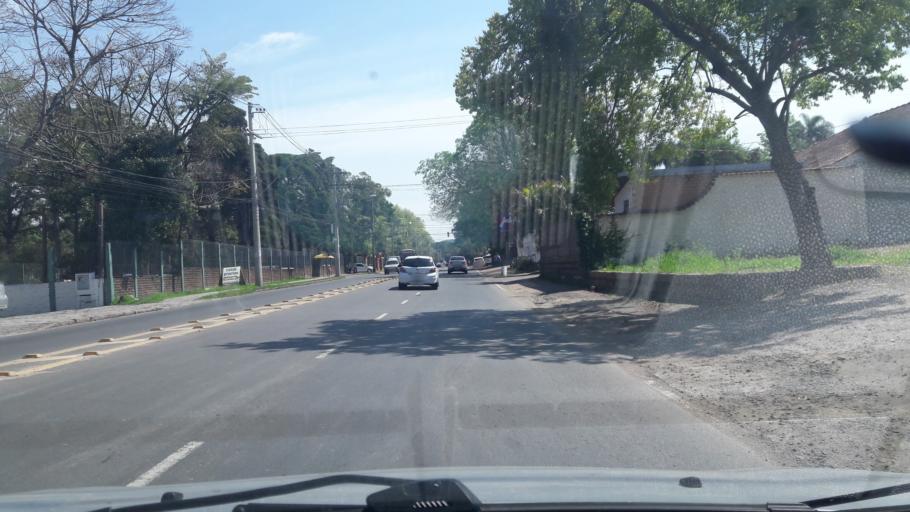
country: BR
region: Rio Grande do Sul
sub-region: Guaiba
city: Guaiba
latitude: -30.1302
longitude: -51.2383
